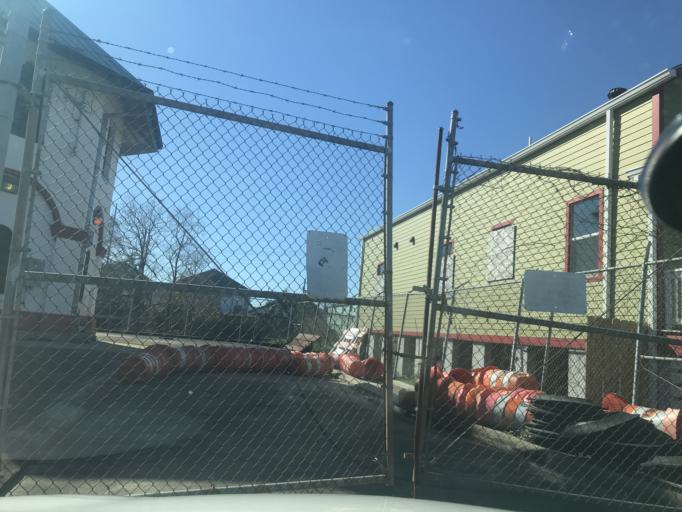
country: US
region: Louisiana
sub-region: Orleans Parish
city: New Orleans
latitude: 29.9527
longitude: -90.0962
